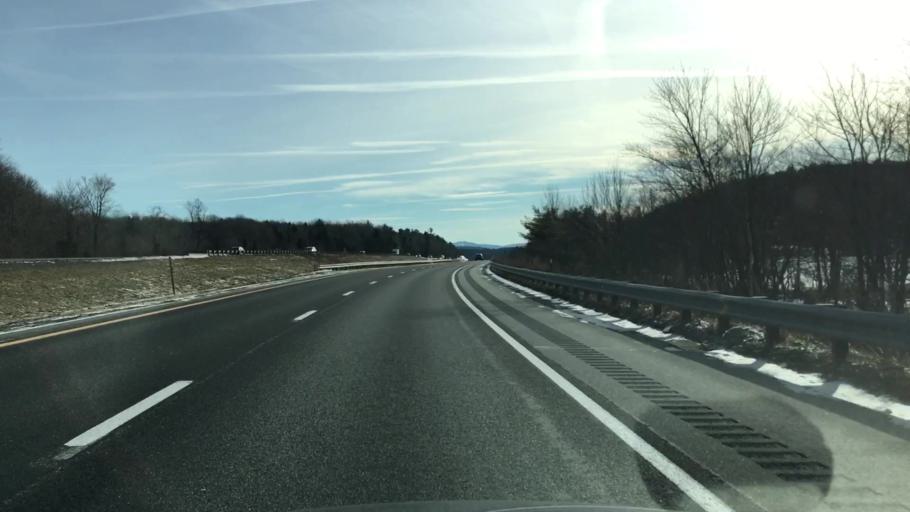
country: US
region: New Hampshire
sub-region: Sullivan County
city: Grantham
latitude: 43.5603
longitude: -72.1427
